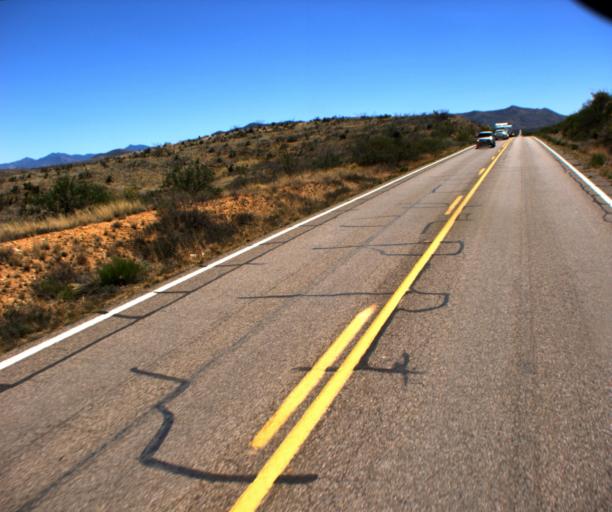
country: US
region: Arizona
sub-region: Pima County
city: Vail
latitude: 31.9752
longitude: -110.6769
